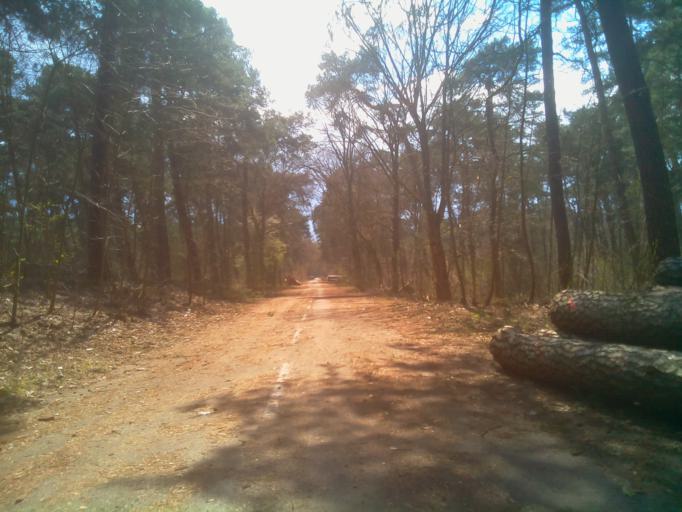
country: DE
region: Baden-Wuerttemberg
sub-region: Karlsruhe Region
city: Ilvesheim
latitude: 49.4396
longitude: 8.5593
